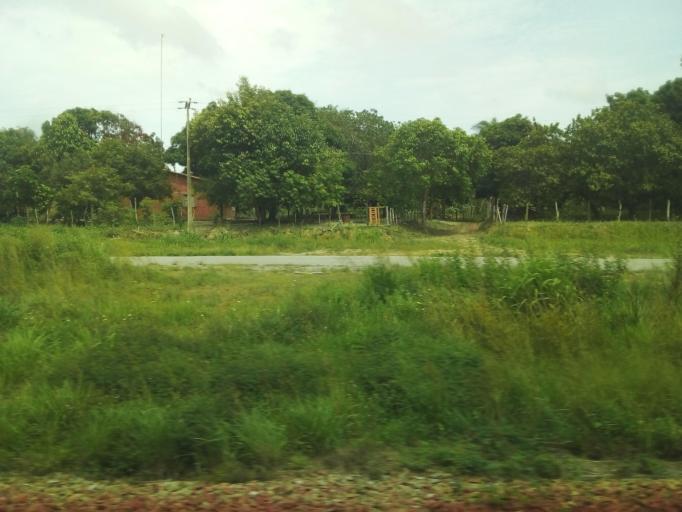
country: BR
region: Maranhao
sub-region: Arari
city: Arari
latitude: -3.5160
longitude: -44.6274
